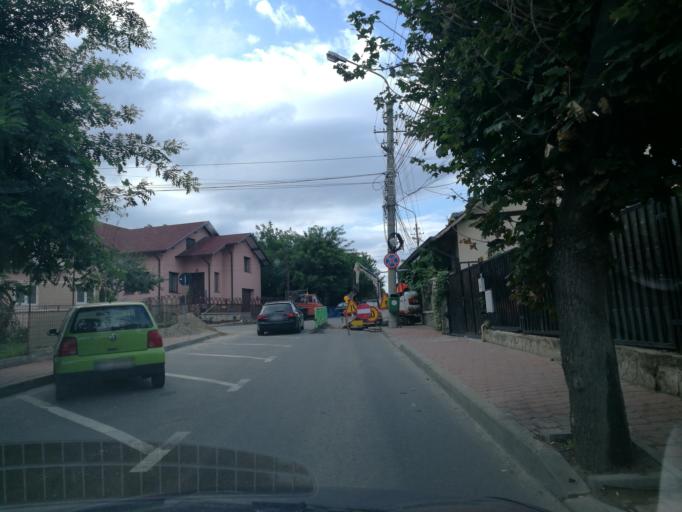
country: RO
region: Suceava
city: Suceava
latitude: 47.6507
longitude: 26.2548
